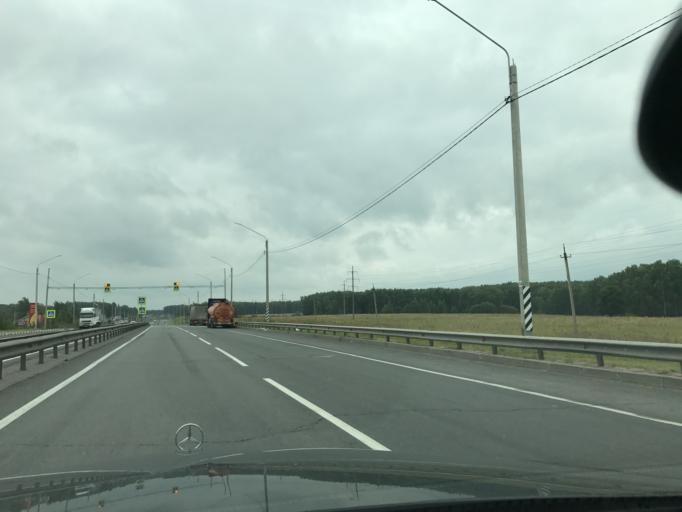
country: RU
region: Vladimir
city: Vyazniki
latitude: 56.2321
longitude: 42.1164
